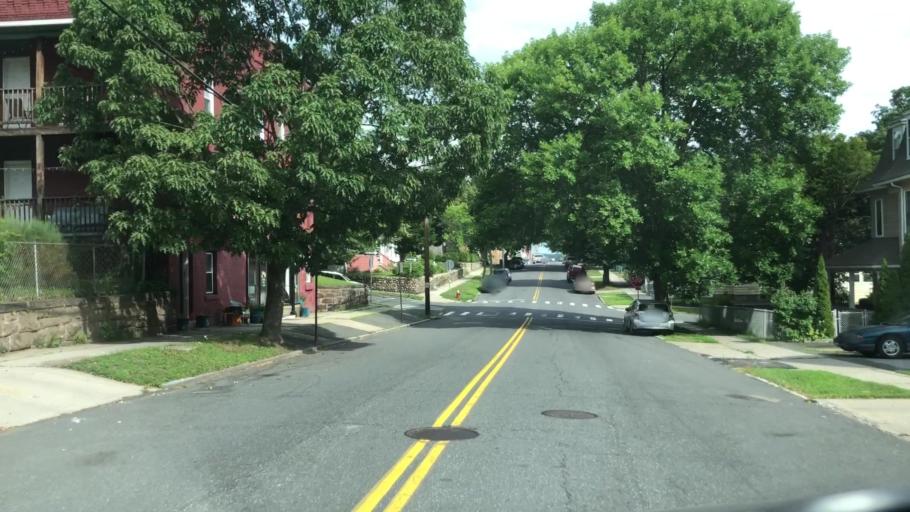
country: US
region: Massachusetts
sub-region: Hampden County
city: Holyoke
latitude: 42.2045
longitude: -72.6217
